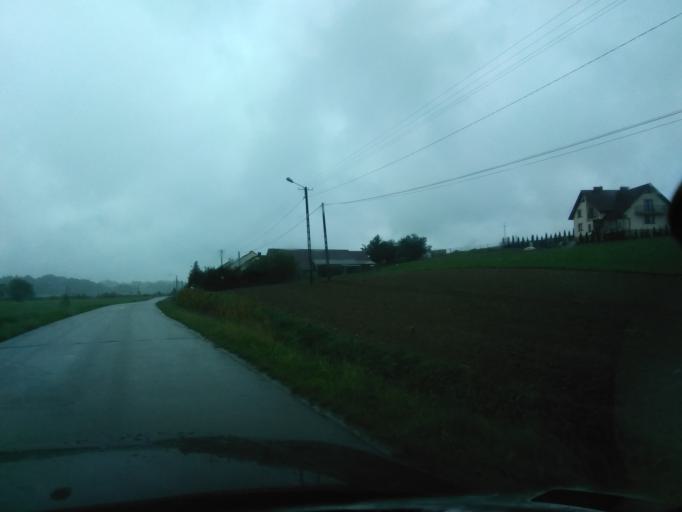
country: PL
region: Subcarpathian Voivodeship
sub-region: Powiat ropczycko-sedziszowski
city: Niedzwiada
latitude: 49.9985
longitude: 21.5530
